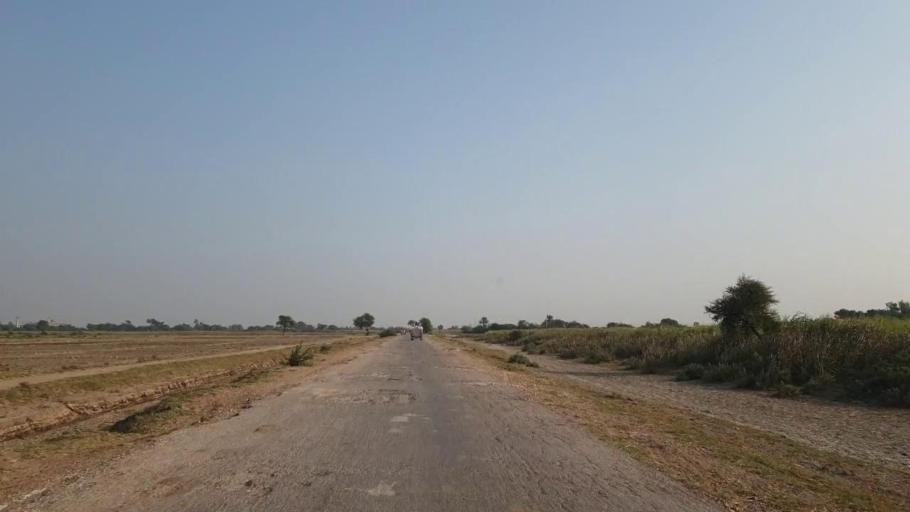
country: PK
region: Sindh
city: Bulri
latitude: 24.9734
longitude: 68.4017
